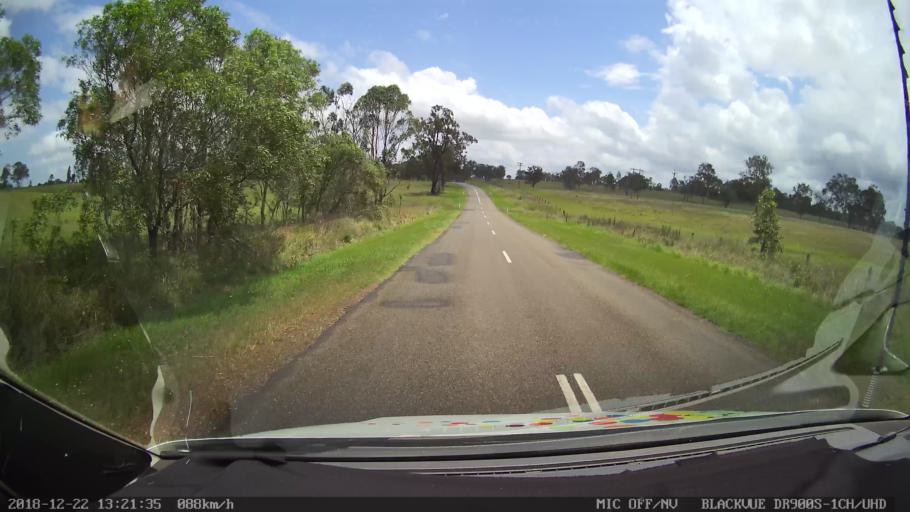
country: AU
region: New South Wales
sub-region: Clarence Valley
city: Coutts Crossing
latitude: -29.7784
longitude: 152.9189
